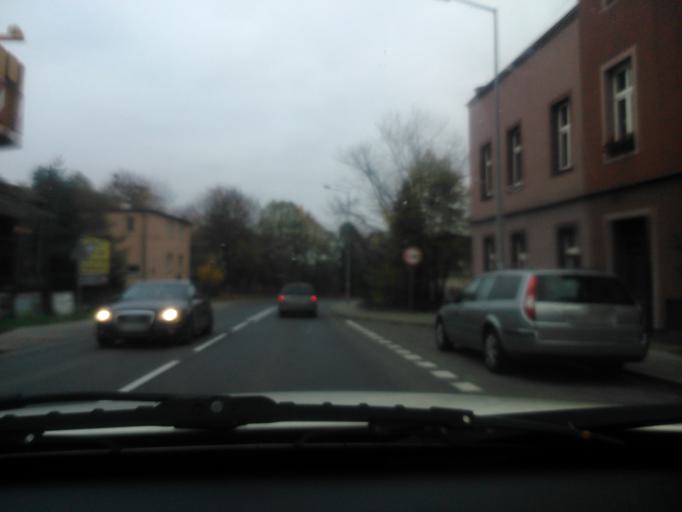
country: PL
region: Kujawsko-Pomorskie
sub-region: Powiat golubsko-dobrzynski
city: Golub-Dobrzyn
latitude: 53.1160
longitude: 19.0525
